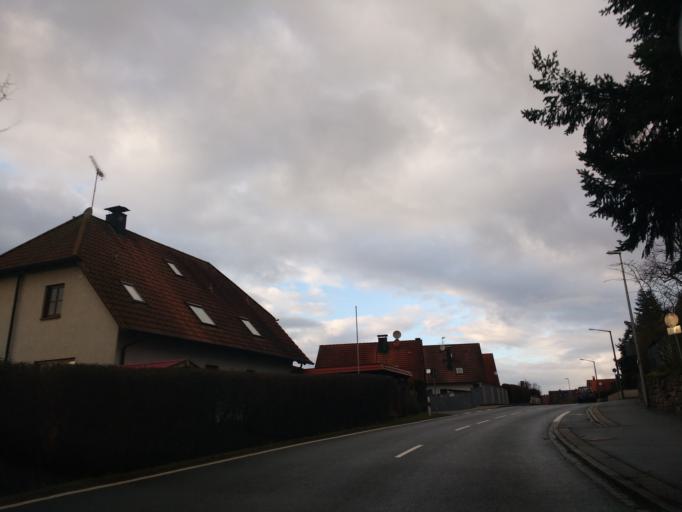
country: DE
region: Bavaria
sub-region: Regierungsbezirk Mittelfranken
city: Herzogenaurach
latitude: 49.5910
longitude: 10.8539
